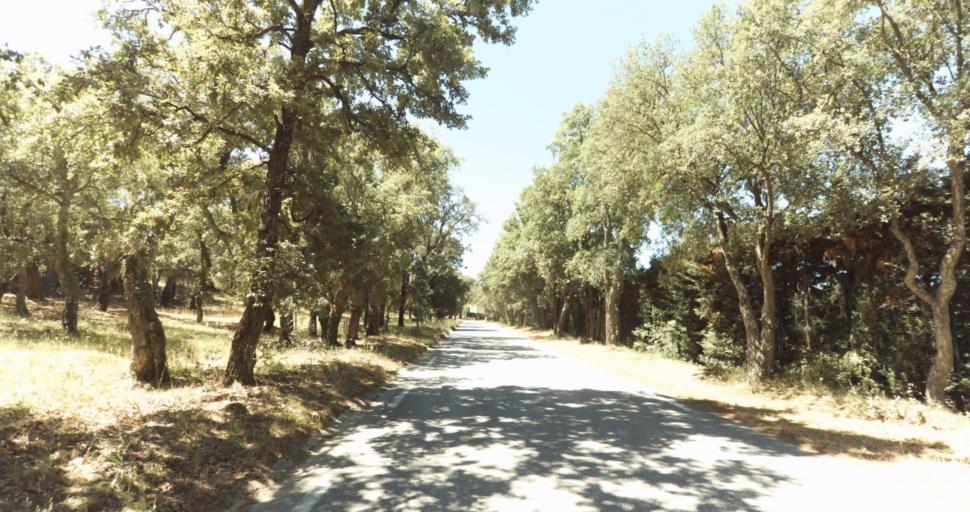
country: FR
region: Provence-Alpes-Cote d'Azur
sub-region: Departement du Var
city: Gassin
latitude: 43.2516
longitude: 6.5825
